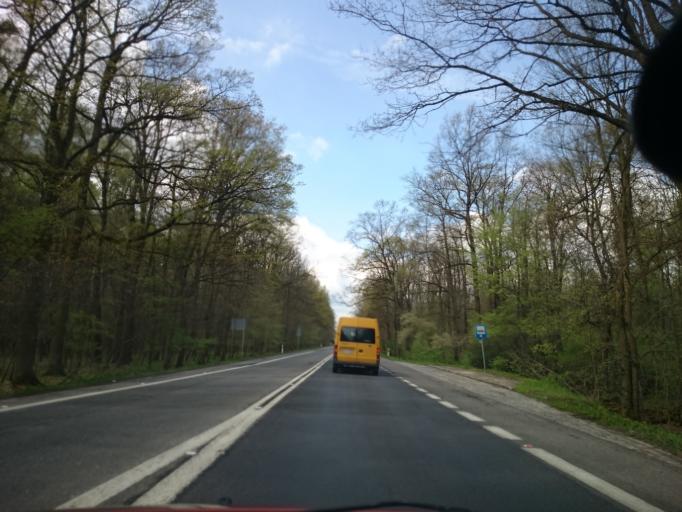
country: PL
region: Opole Voivodeship
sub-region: Powiat opolski
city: Tarnow Opolski
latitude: 50.5964
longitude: 18.0906
